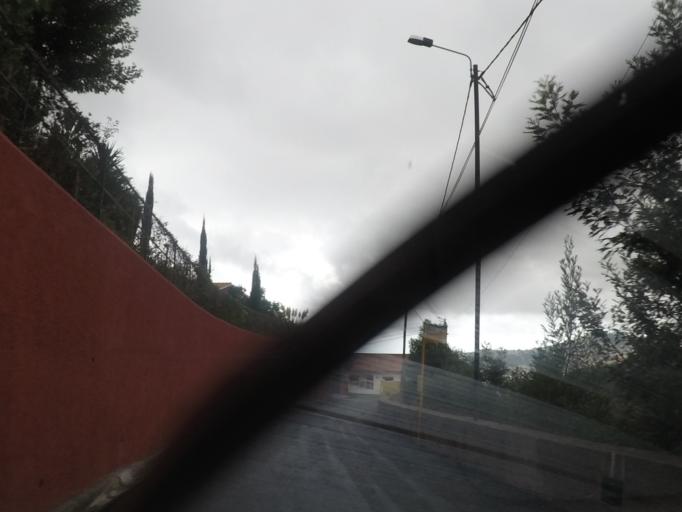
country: PT
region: Madeira
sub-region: Funchal
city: Nossa Senhora do Monte
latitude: 32.6741
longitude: -16.9134
